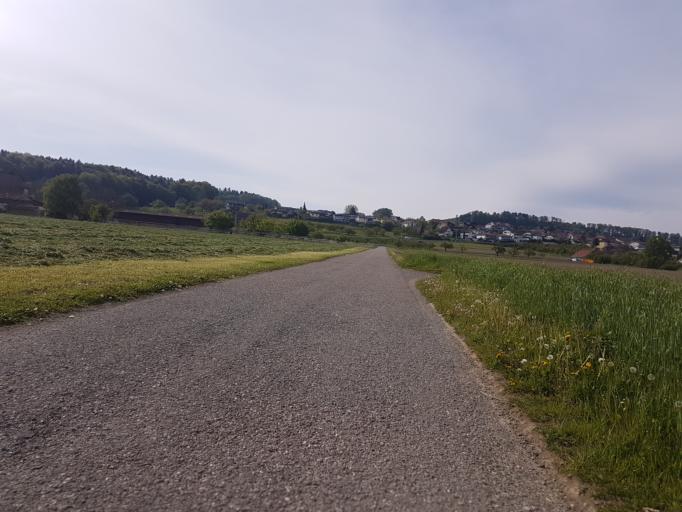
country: CH
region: Bern
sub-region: Seeland District
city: Tauffelen
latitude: 47.0912
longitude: 7.2126
